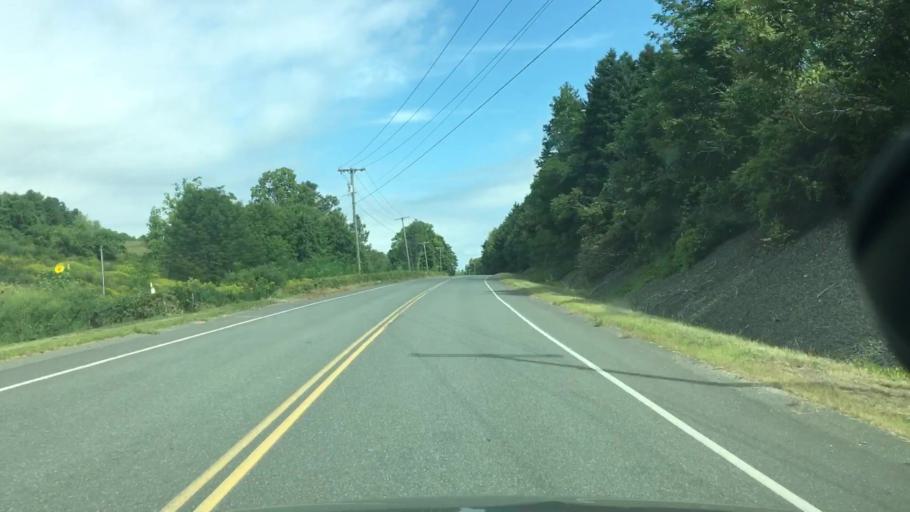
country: US
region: Massachusetts
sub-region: Franklin County
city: Colrain
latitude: 42.6439
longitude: -72.6746
